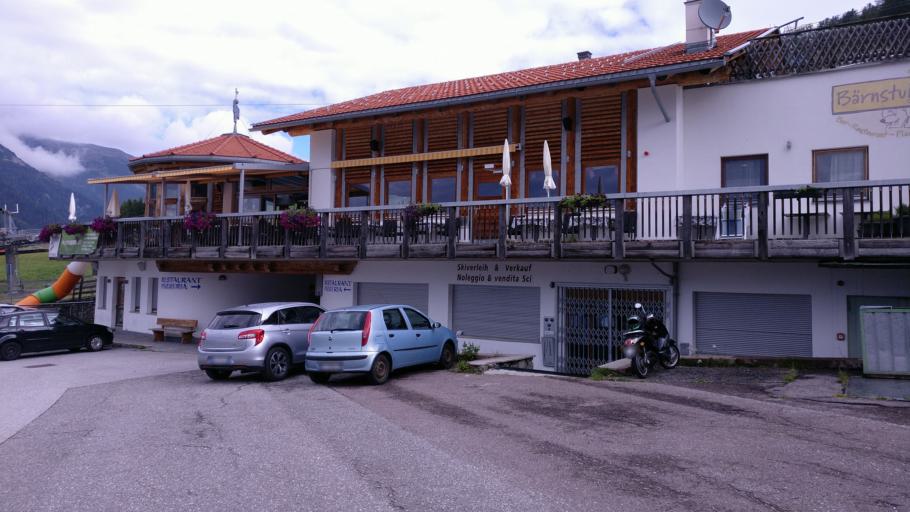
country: IT
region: Trentino-Alto Adige
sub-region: Bolzano
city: Sarentino
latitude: 46.6877
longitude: 11.4214
